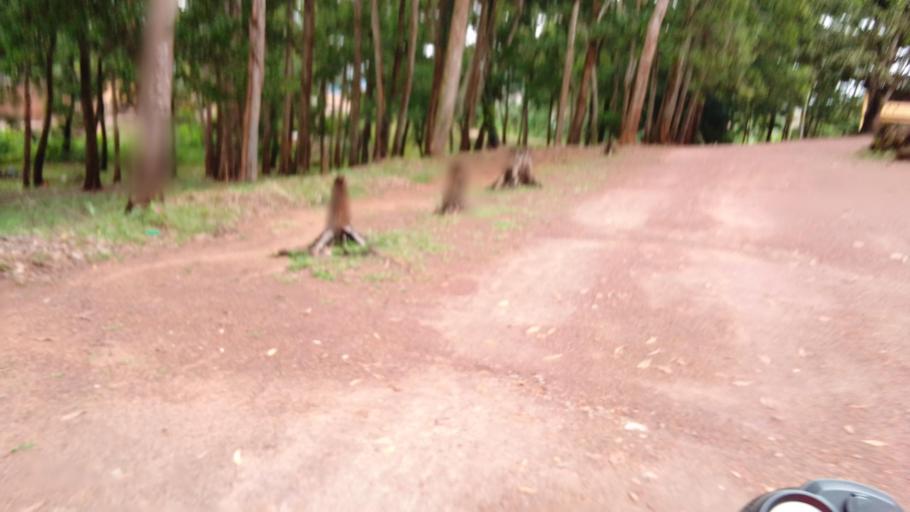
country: SL
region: Eastern Province
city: Kenema
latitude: 7.8808
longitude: -11.1968
